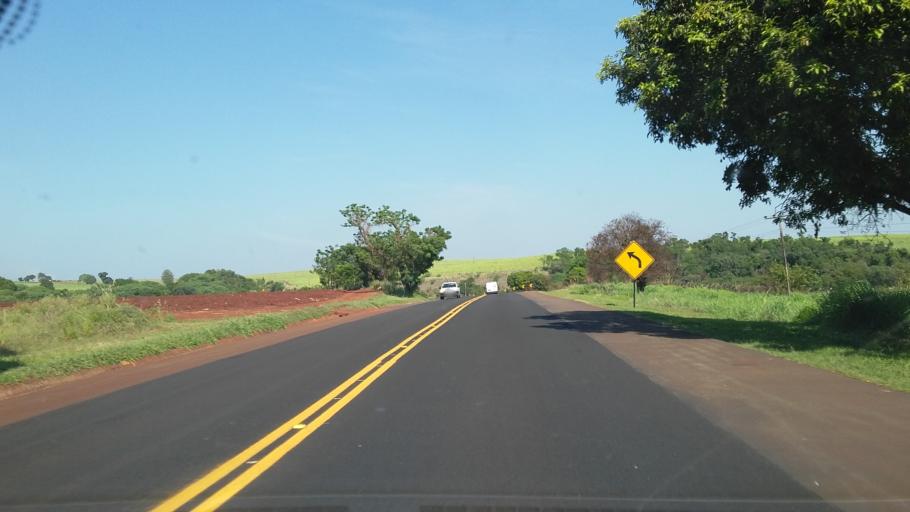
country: BR
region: Parana
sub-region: Bandeirantes
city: Bandeirantes
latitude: -23.1287
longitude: -50.4504
